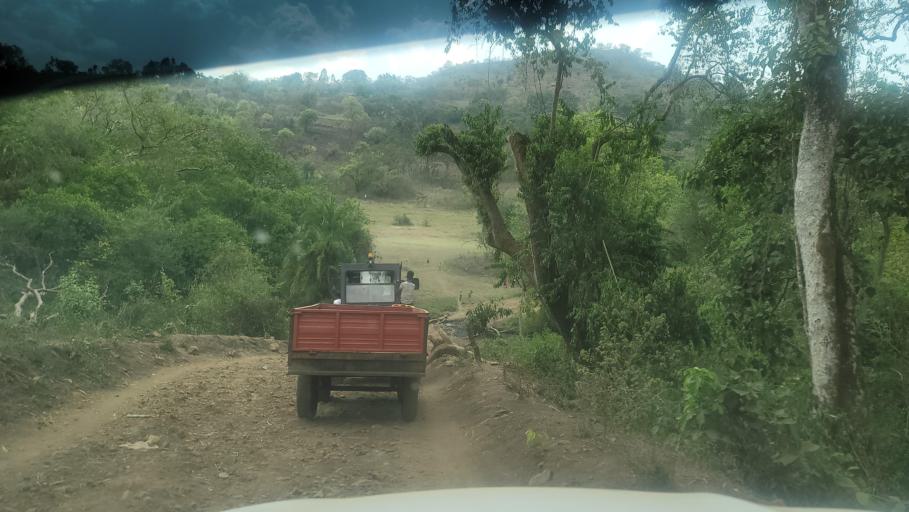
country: ET
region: Southern Nations, Nationalities, and People's Region
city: Bonga
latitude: 7.5120
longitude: 36.2784
